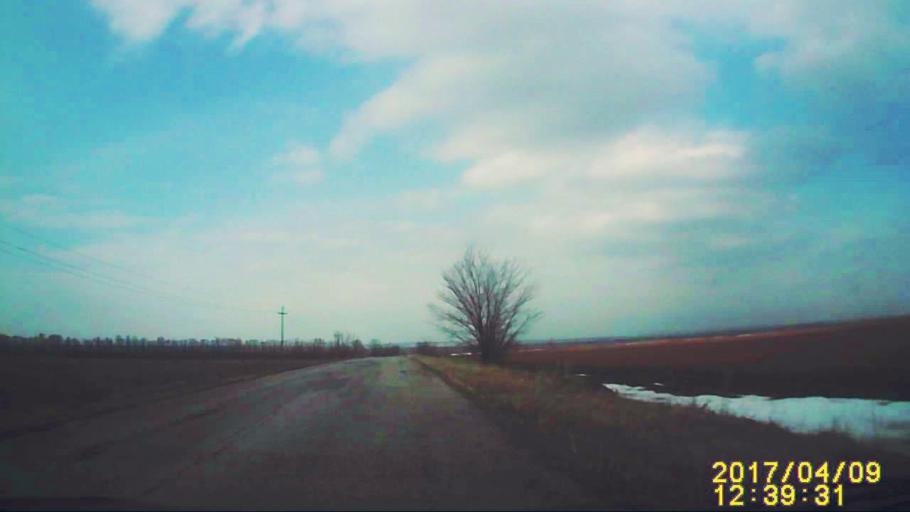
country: RU
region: Ulyanovsk
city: Ignatovka
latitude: 53.9993
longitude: 47.9556
